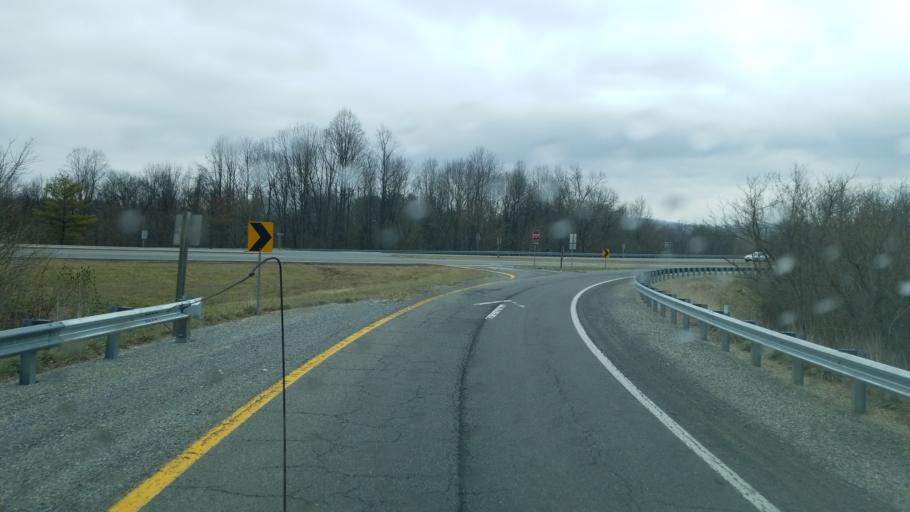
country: US
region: Virginia
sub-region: Giles County
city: Pearisburg
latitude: 37.3349
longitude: -80.7389
